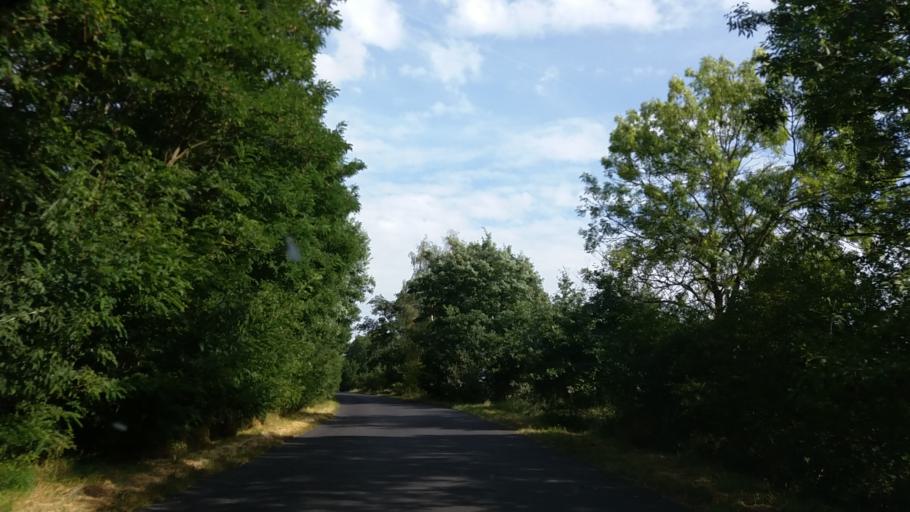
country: PL
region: West Pomeranian Voivodeship
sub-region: Powiat stargardzki
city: Suchan
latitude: 53.2243
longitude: 15.2844
